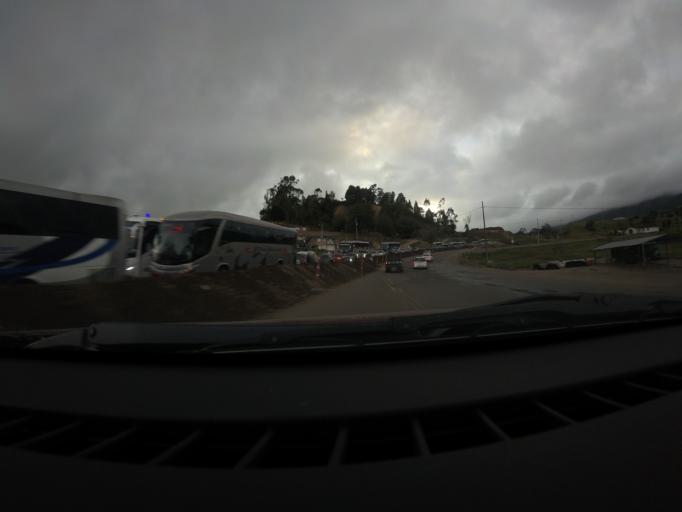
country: CO
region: Boyaca
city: Samaca
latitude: 5.4406
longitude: -73.4388
